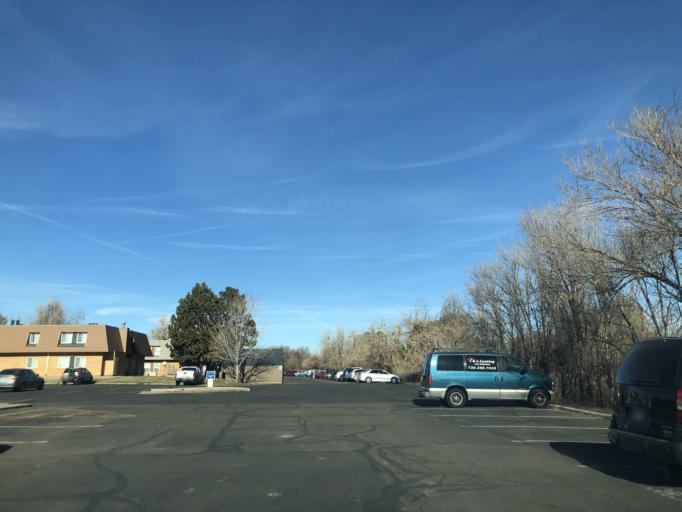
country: US
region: Colorado
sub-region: Adams County
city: Aurora
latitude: 39.7152
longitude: -104.8170
